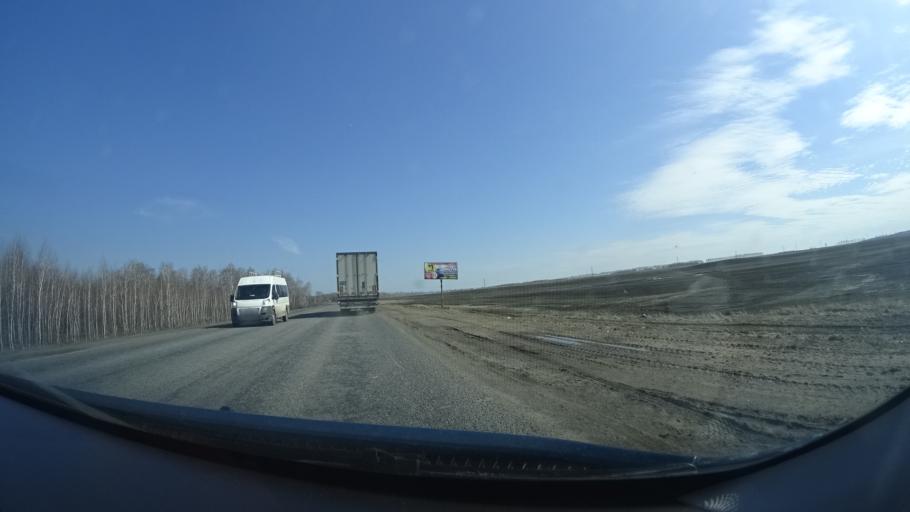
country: RU
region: Bashkortostan
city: Serafimovskiy
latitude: 54.4705
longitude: 53.7885
